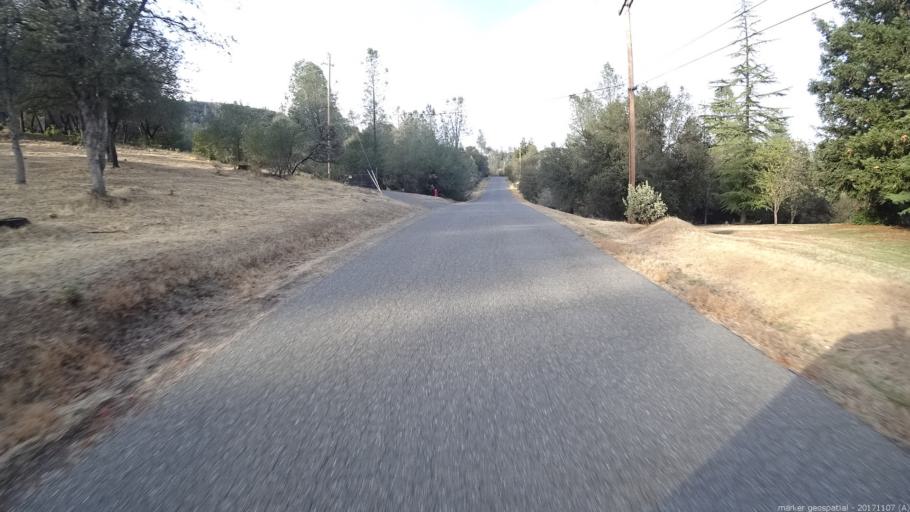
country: US
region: California
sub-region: Shasta County
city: Shasta
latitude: 40.5267
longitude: -122.4859
